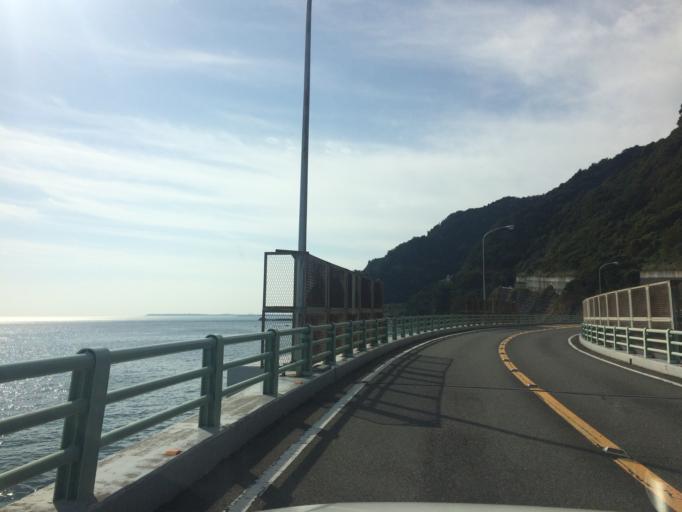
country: JP
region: Shizuoka
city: Yaizu
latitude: 34.9072
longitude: 138.3539
